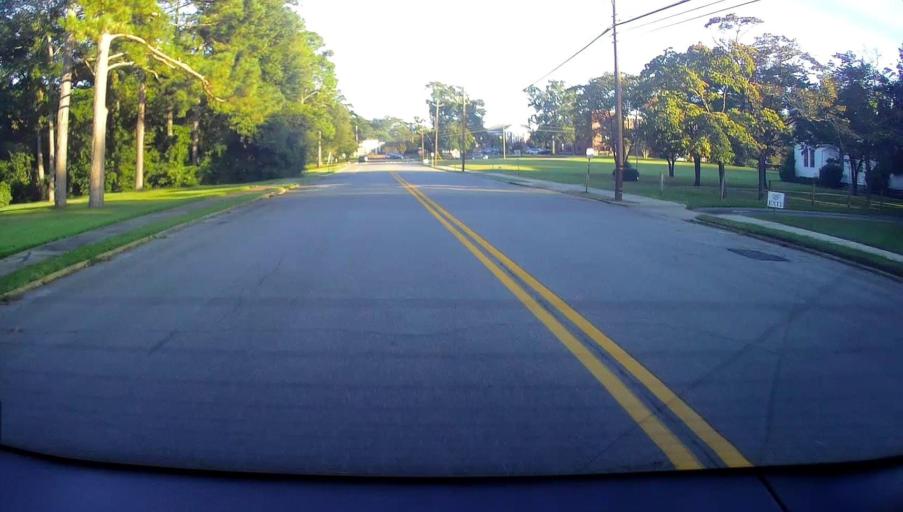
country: US
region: Georgia
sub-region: Bleckley County
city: Cochran
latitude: 32.3826
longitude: -83.3478
